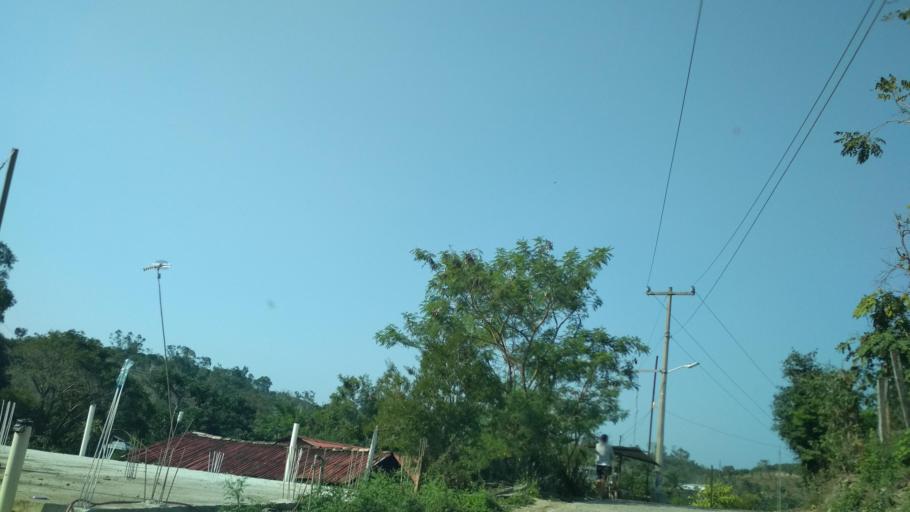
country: MX
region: Veracruz
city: Agua Dulce
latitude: 20.3914
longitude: -97.2115
